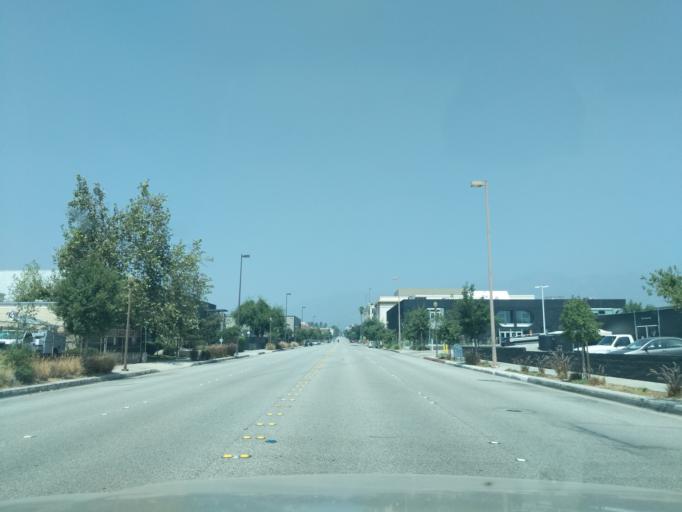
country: US
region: California
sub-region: Los Angeles County
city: South Pasadena
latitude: 34.1304
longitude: -118.1488
